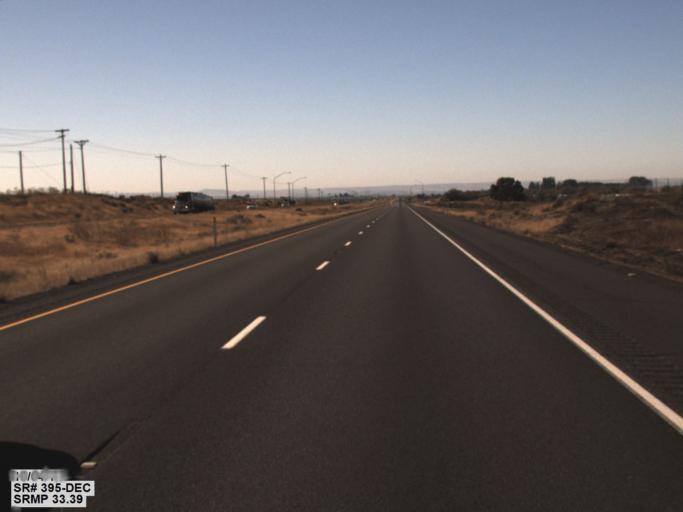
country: US
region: Washington
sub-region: Franklin County
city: Pasco
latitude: 46.3996
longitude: -119.0577
